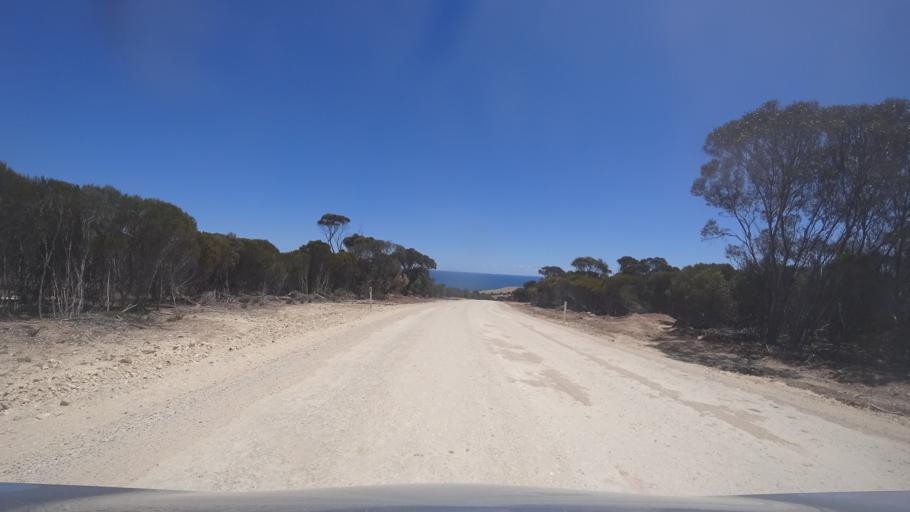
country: AU
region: South Australia
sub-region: Kangaroo Island
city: Kingscote
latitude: -35.6312
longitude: 137.2138
